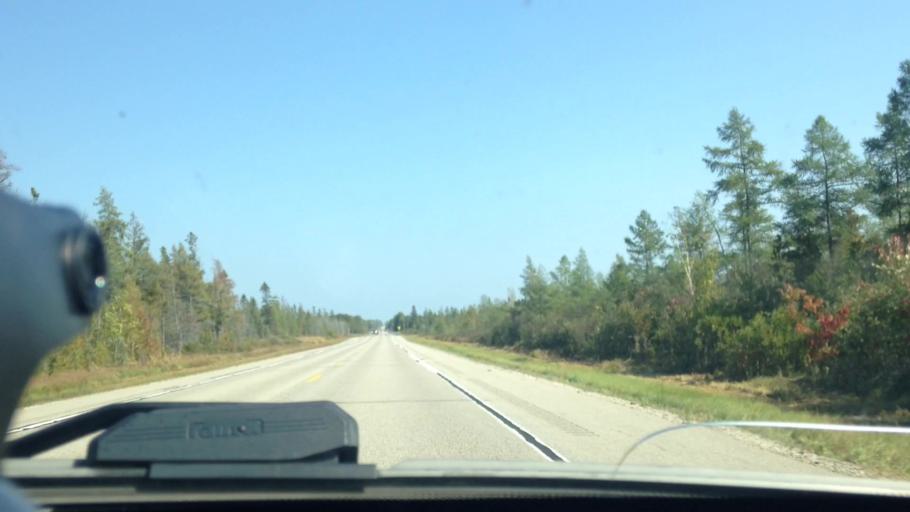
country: US
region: Michigan
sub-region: Luce County
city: Newberry
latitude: 46.3035
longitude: -85.3313
